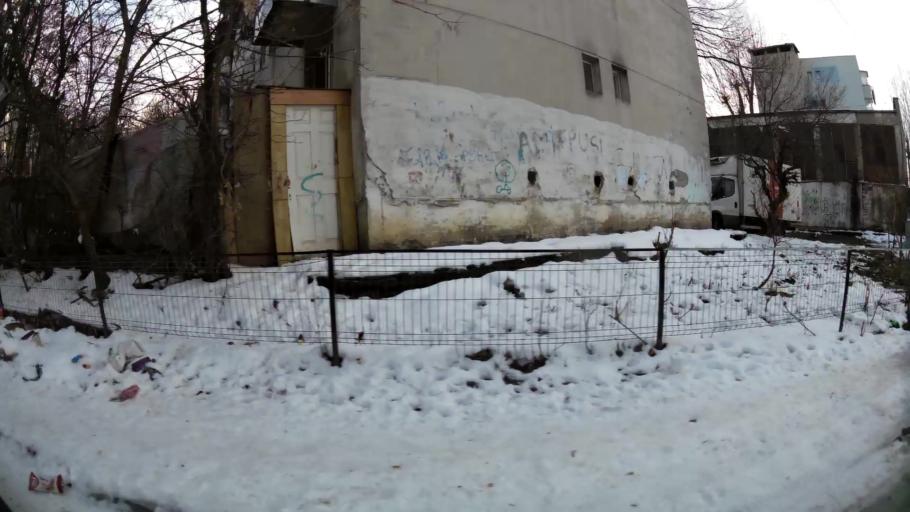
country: RO
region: Bucuresti
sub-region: Municipiul Bucuresti
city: Bucuresti
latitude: 44.3907
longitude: 26.0744
